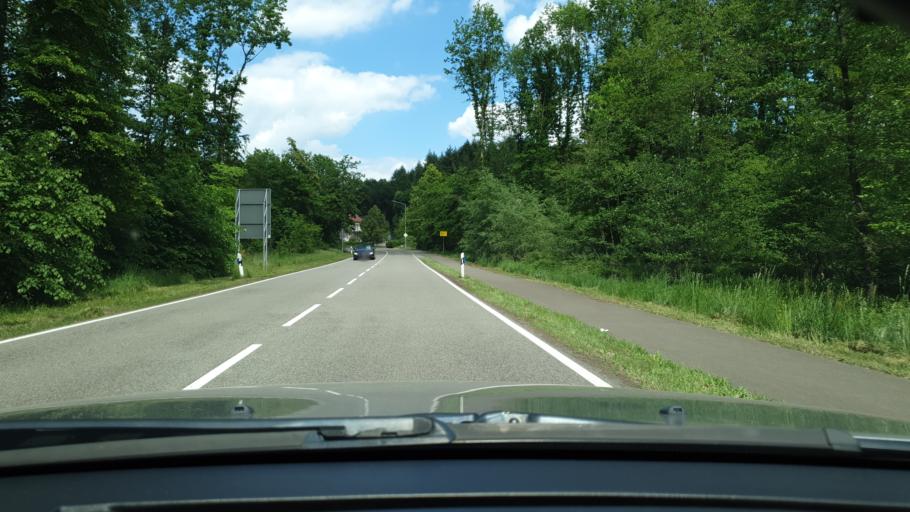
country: DE
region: Saarland
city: Homburg
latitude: 49.3331
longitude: 7.3665
